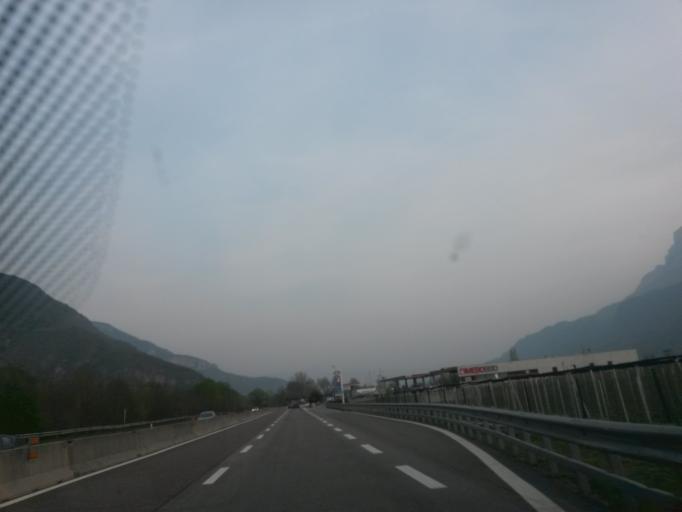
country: IT
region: Trentino-Alto Adige
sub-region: Bolzano
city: Gargazzone
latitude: 46.5655
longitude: 11.2129
